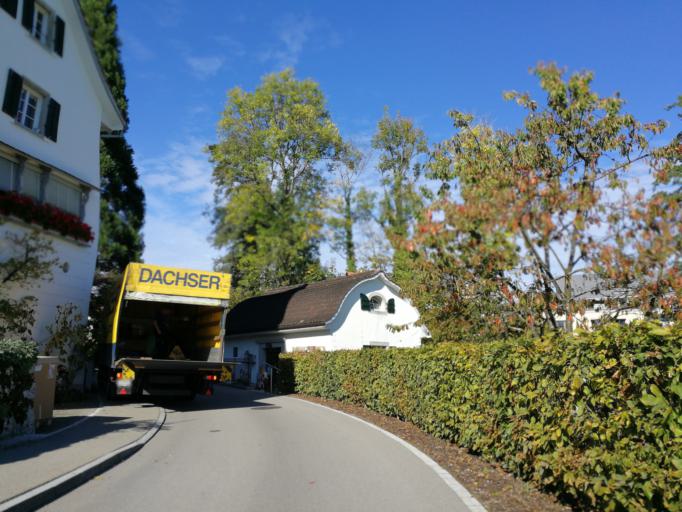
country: CH
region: Zurich
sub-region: Bezirk Meilen
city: Hombrechtikon
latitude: 47.2457
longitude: 8.7727
